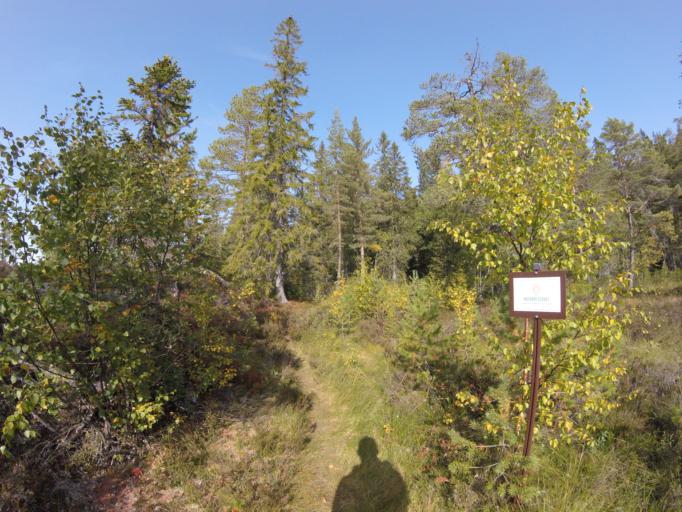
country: NO
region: Buskerud
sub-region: Kongsberg
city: Kongsberg
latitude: 59.6530
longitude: 9.5107
